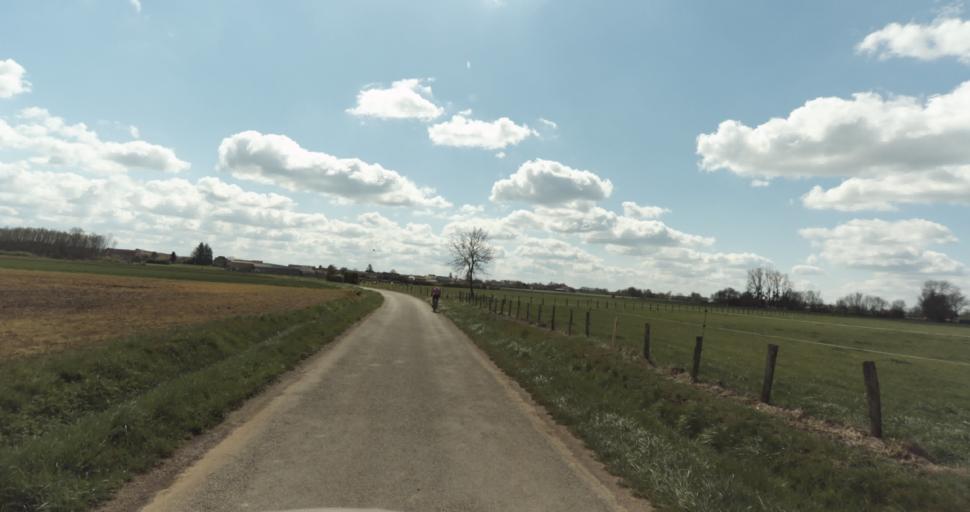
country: FR
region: Bourgogne
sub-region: Departement de la Cote-d'Or
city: Auxonne
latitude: 47.2129
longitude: 5.4060
